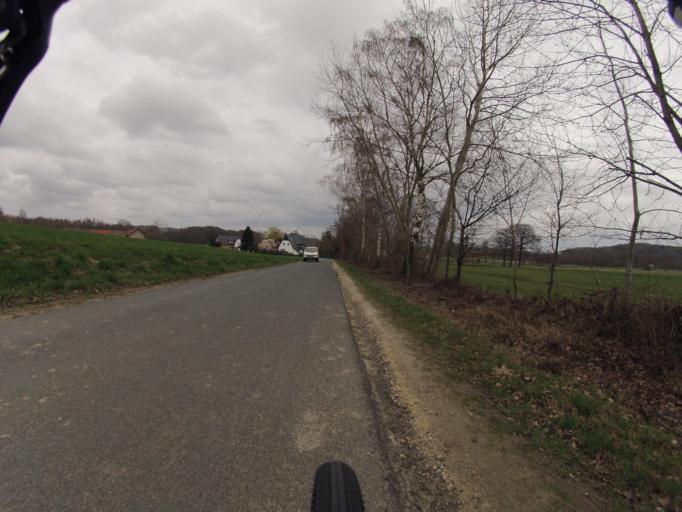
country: DE
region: North Rhine-Westphalia
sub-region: Regierungsbezirk Munster
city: Mettingen
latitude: 52.2948
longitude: 7.8225
